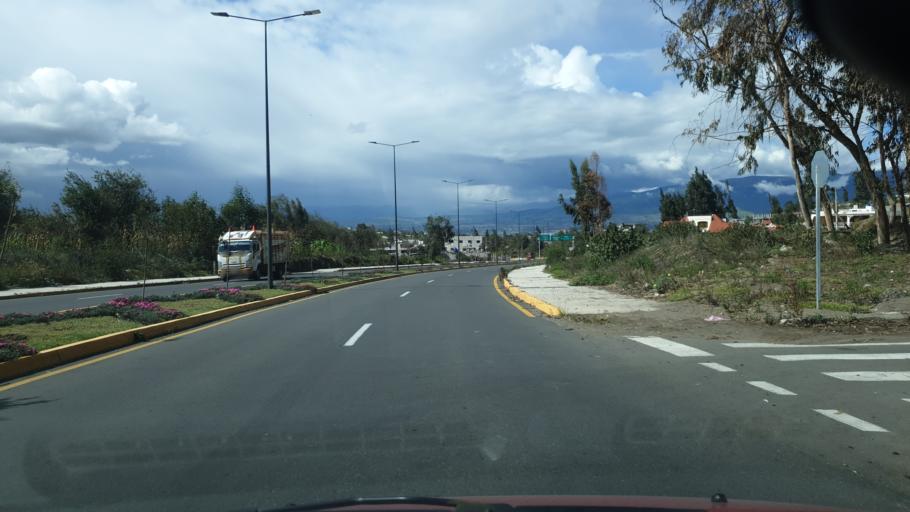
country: EC
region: Tungurahua
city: Ambato
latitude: -1.2919
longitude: -78.6317
